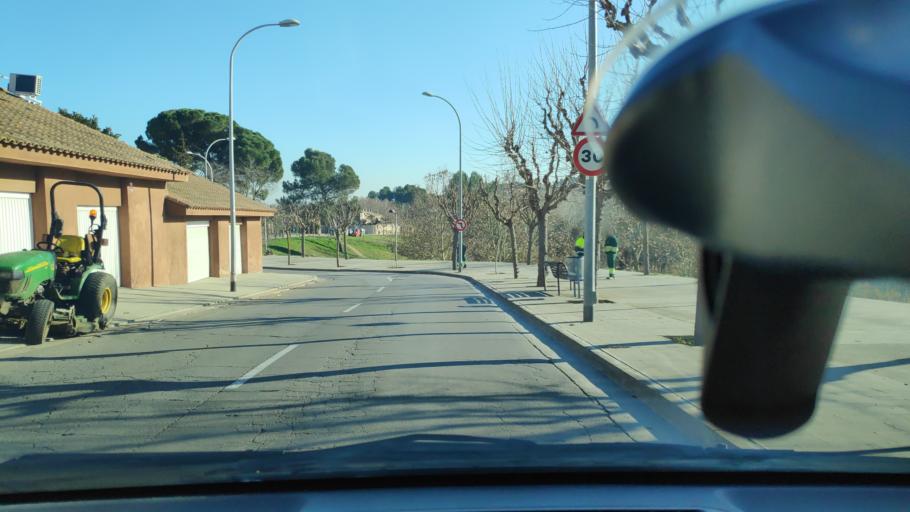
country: ES
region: Catalonia
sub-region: Provincia de Barcelona
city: Sant Quirze del Valles
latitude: 41.5330
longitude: 2.0719
